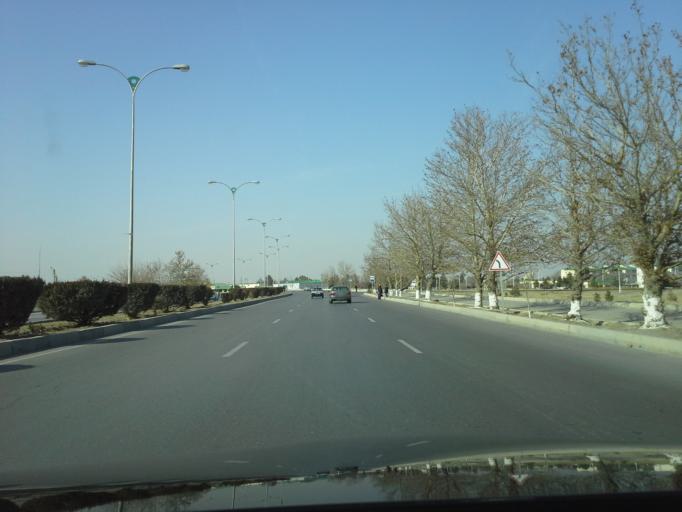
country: TM
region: Ahal
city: Abadan
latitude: 38.0539
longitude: 58.1831
